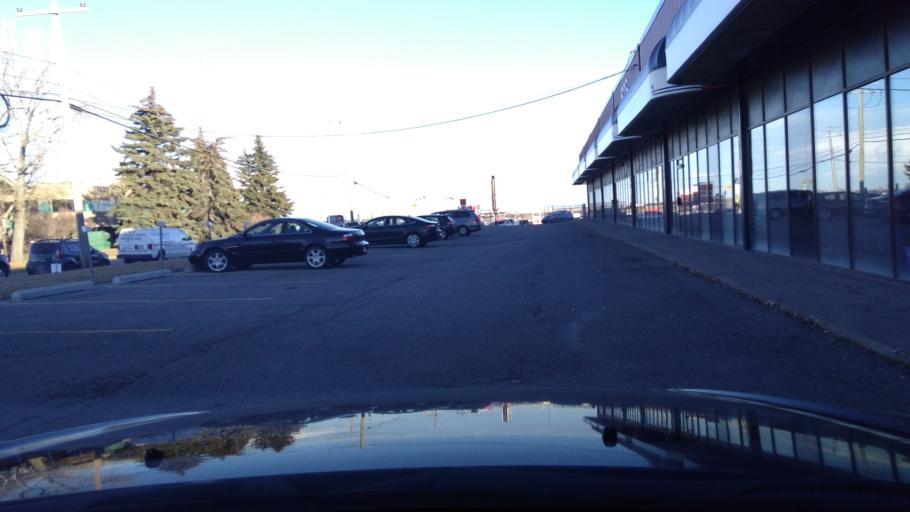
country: CA
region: Alberta
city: Calgary
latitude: 50.9843
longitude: -114.0503
